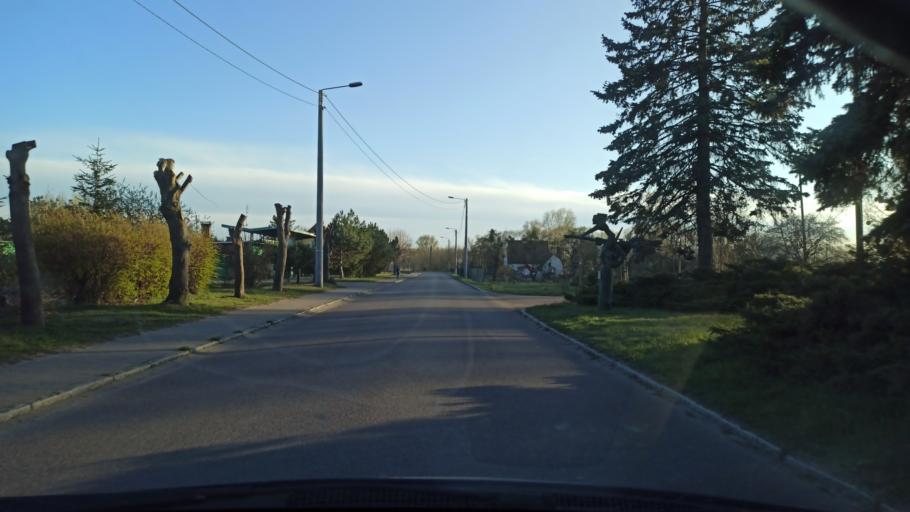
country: PL
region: Warmian-Masurian Voivodeship
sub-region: Powiat elblaski
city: Tolkmicko
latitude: 54.3216
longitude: 19.5236
